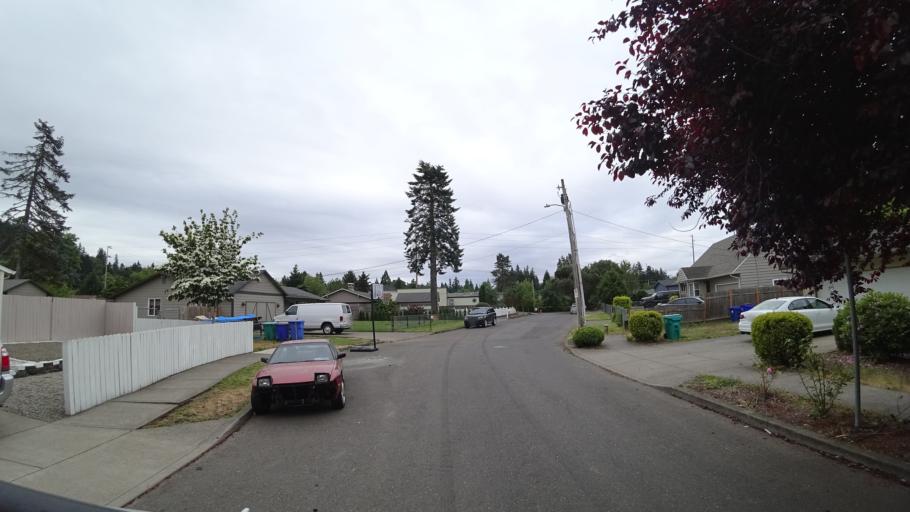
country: US
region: Oregon
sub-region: Multnomah County
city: Lents
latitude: 45.4905
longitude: -122.5249
